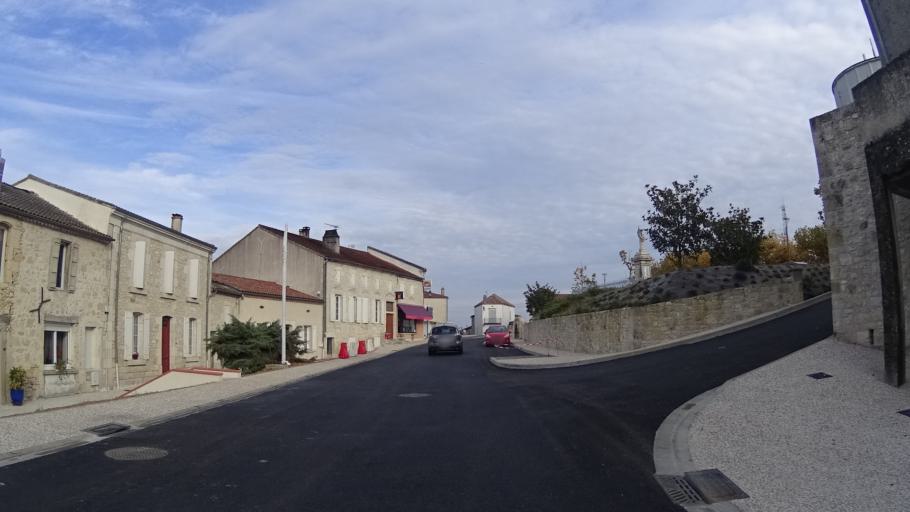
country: FR
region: Aquitaine
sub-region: Departement du Lot-et-Garonne
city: Laplume
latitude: 44.1125
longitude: 0.5300
